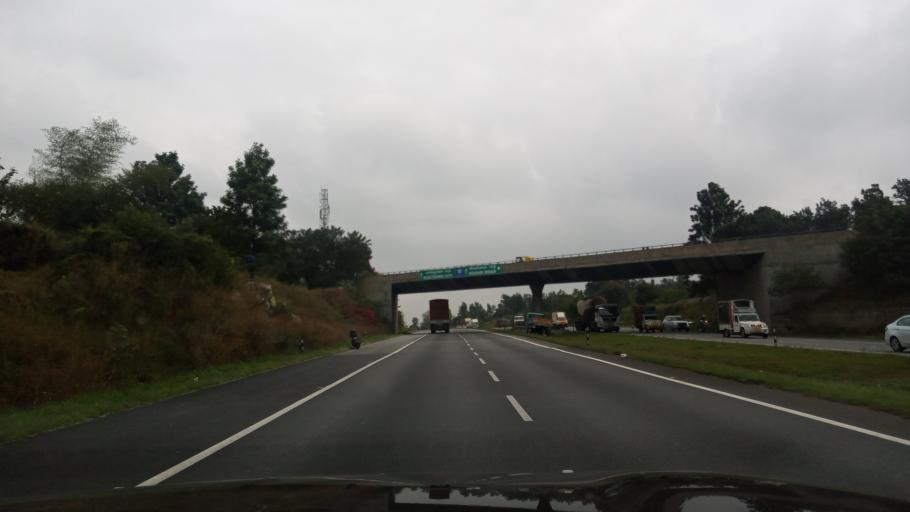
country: IN
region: Karnataka
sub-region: Bangalore Urban
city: Bangalore
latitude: 12.8548
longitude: 77.6089
